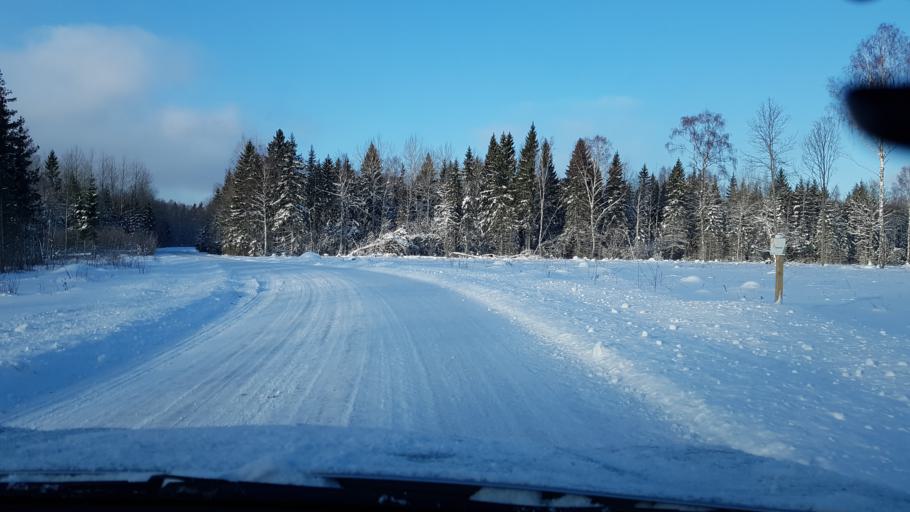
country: EE
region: Harju
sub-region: Nissi vald
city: Turba
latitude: 59.1184
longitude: 24.2211
